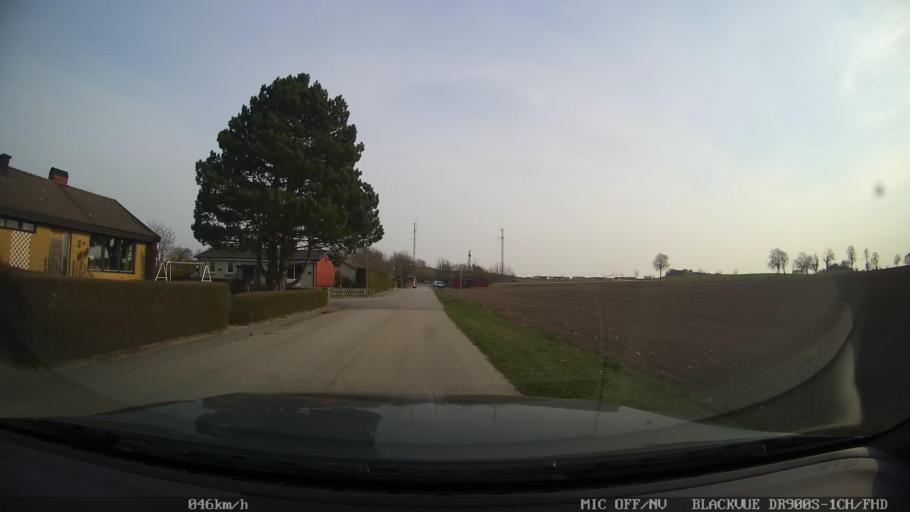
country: SE
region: Skane
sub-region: Ystads Kommun
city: Ystad
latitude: 55.4517
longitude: 13.7955
